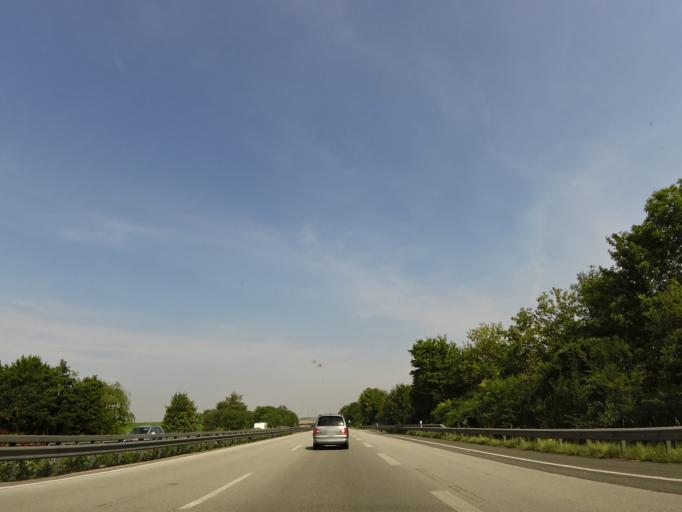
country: DE
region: Rheinland-Pfalz
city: Gundheim
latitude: 49.6880
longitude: 8.2412
